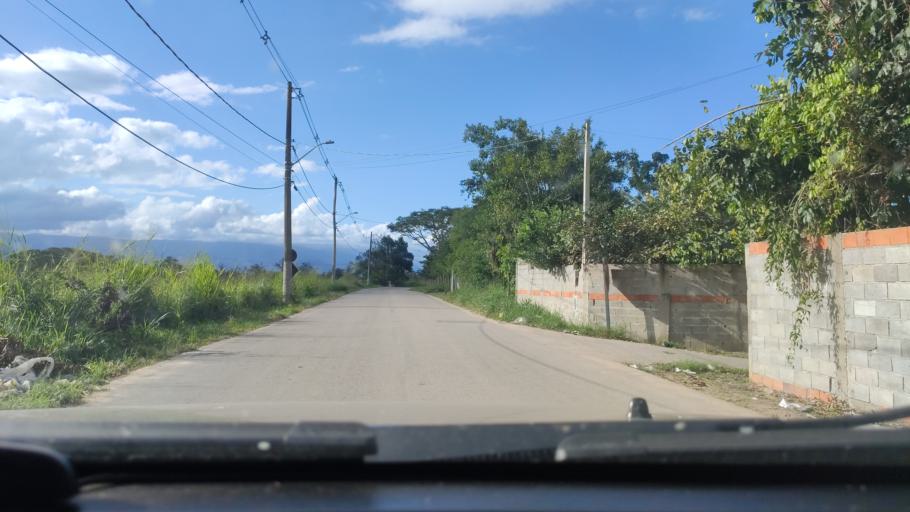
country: BR
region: Sao Paulo
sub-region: Sao Sebastiao
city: Sao Sebastiao
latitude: -23.6939
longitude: -45.4601
